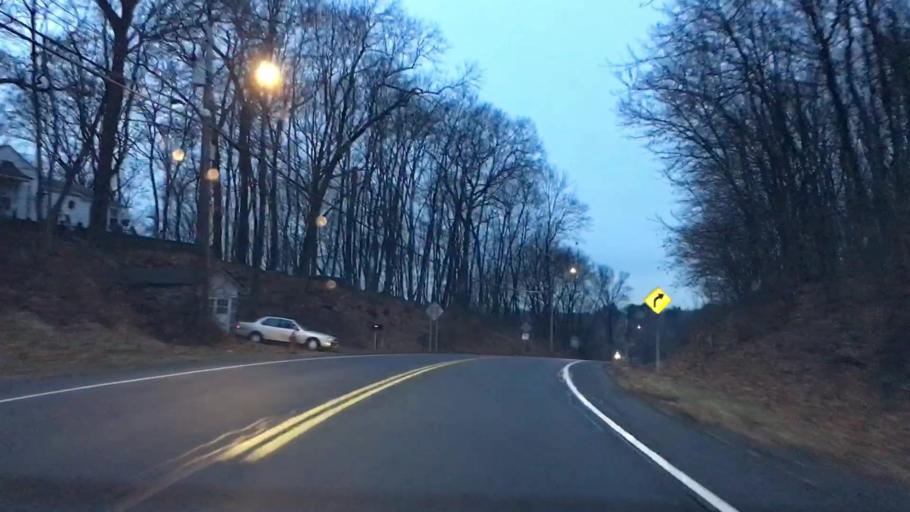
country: US
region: New York
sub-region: Dutchess County
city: Red Oaks Mill
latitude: 41.6716
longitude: -73.8847
